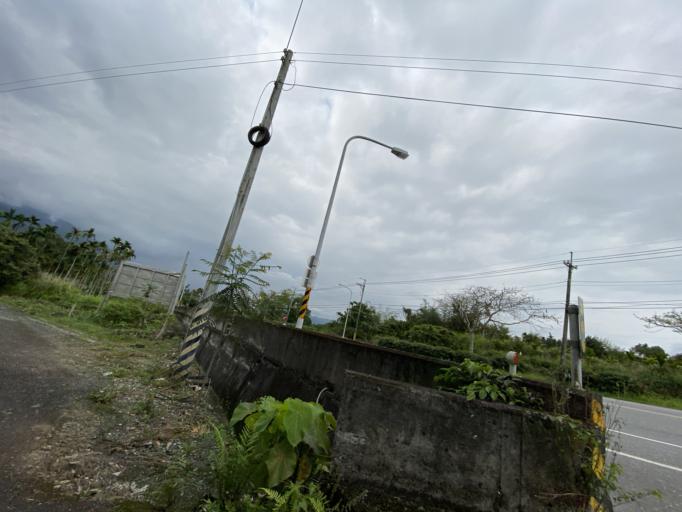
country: TW
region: Taiwan
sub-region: Hualien
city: Hualian
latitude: 23.4693
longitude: 121.3597
